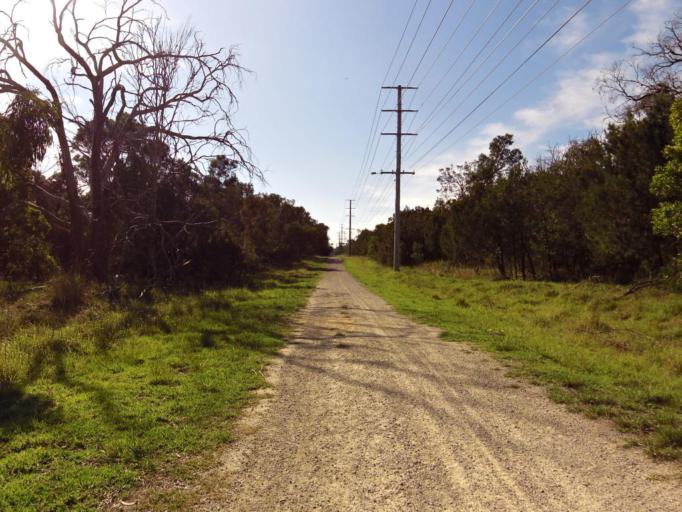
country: AU
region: Victoria
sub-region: Casey
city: Endeavour Hills
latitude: -37.9557
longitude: 145.2456
